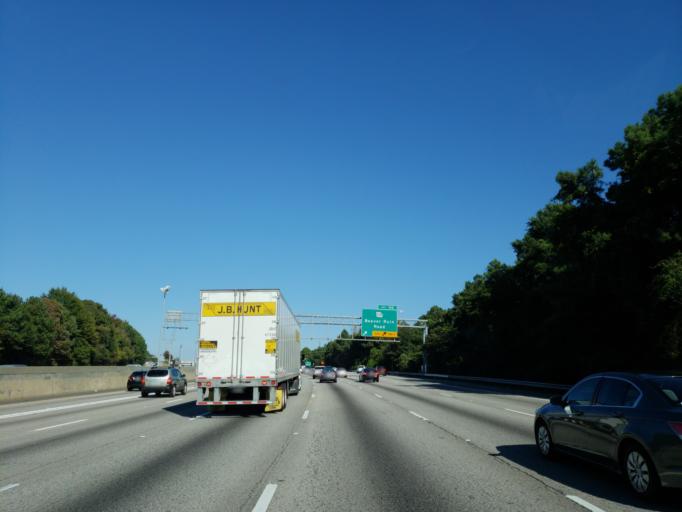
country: US
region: Georgia
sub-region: Gwinnett County
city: Lilburn
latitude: 33.9334
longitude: -84.1636
